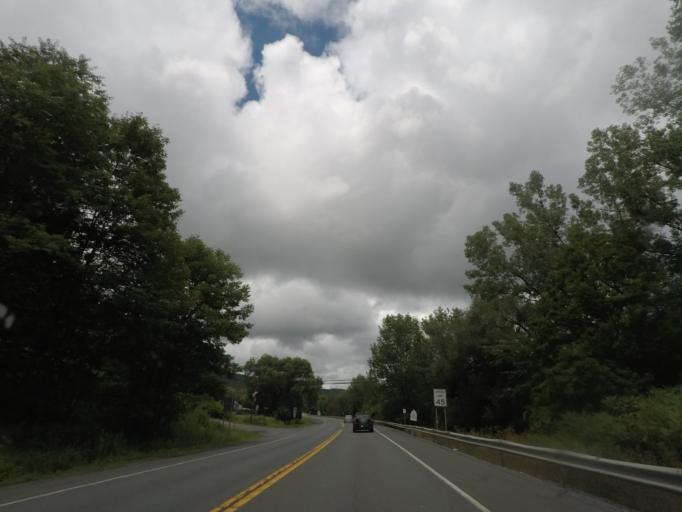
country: US
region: Massachusetts
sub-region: Berkshire County
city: Williamstown
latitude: 42.6891
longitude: -73.3691
